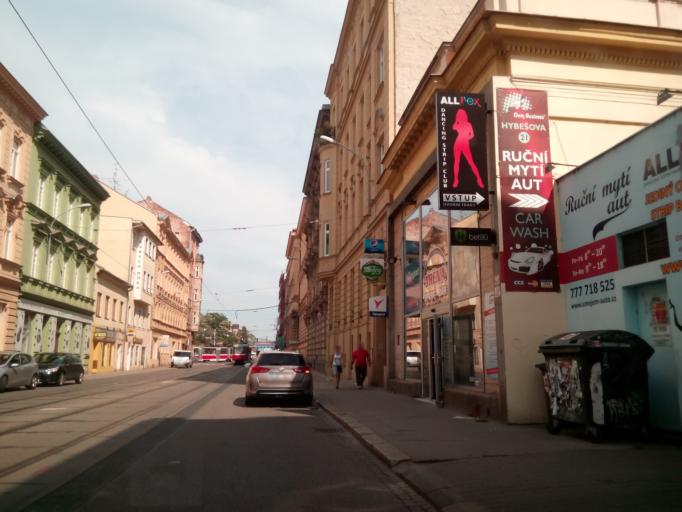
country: CZ
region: South Moravian
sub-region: Mesto Brno
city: Brno
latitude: 49.1892
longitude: 16.6047
